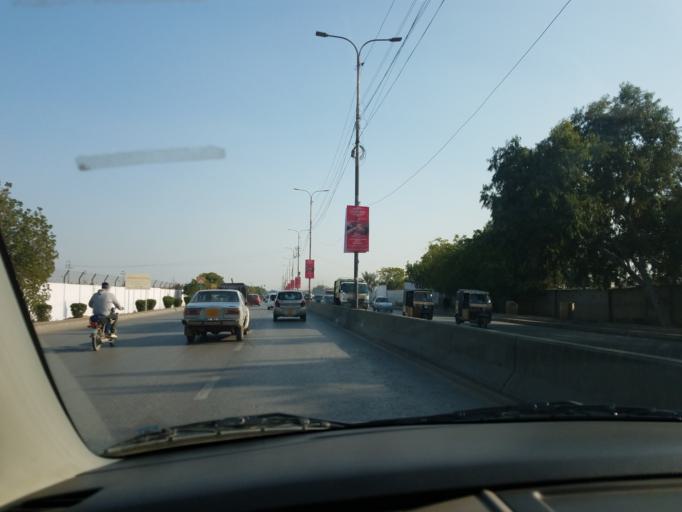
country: PK
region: Sindh
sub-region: Karachi District
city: Karachi
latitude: 24.8940
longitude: 67.1205
